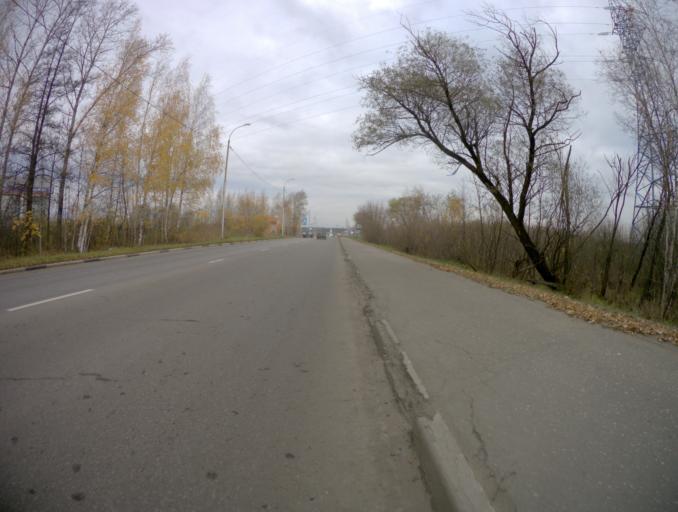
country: RU
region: Moskovskaya
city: Orekhovo-Zuyevo
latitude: 55.8359
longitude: 38.9730
